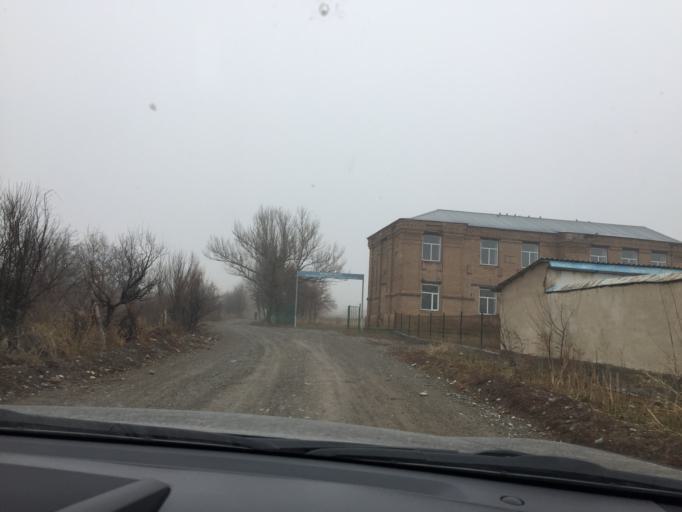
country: KZ
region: Ongtustik Qazaqstan
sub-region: Tulkibas Audany
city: Zhabagly
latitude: 42.5123
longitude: 70.5621
